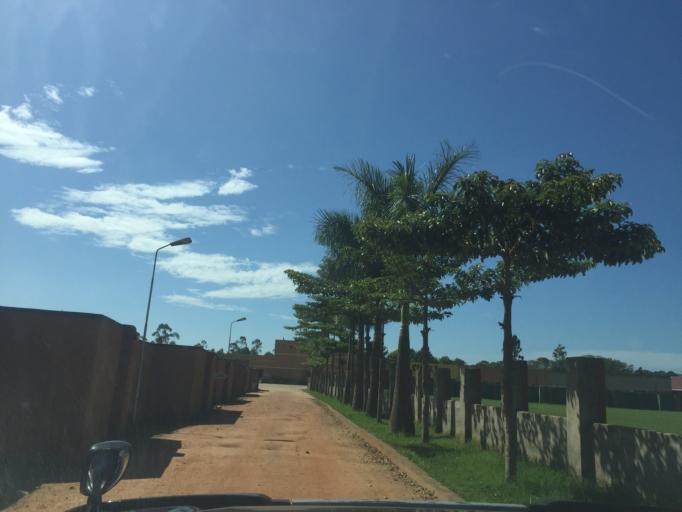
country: UG
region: Central Region
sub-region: Luwero District
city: Luwero
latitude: 0.8448
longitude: 32.5111
